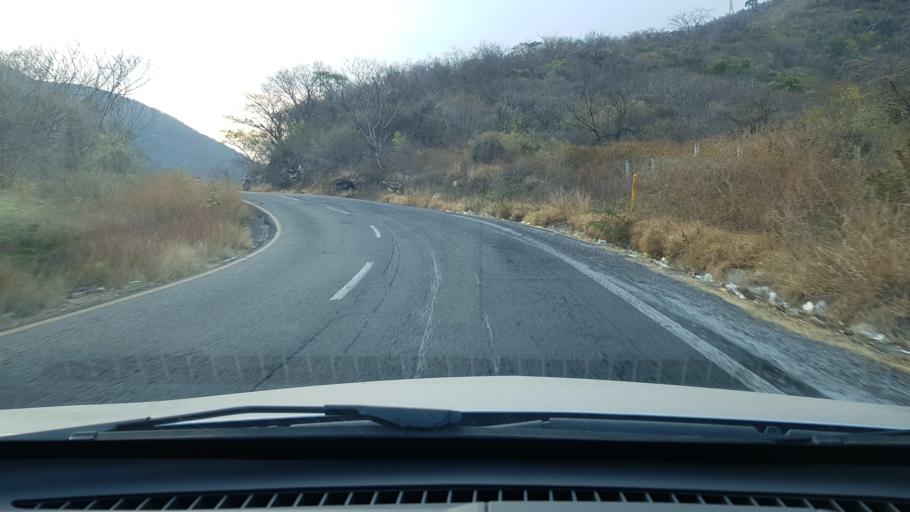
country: MX
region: Morelos
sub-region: Jiutepec
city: Independencia
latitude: 18.8581
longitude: -99.1159
